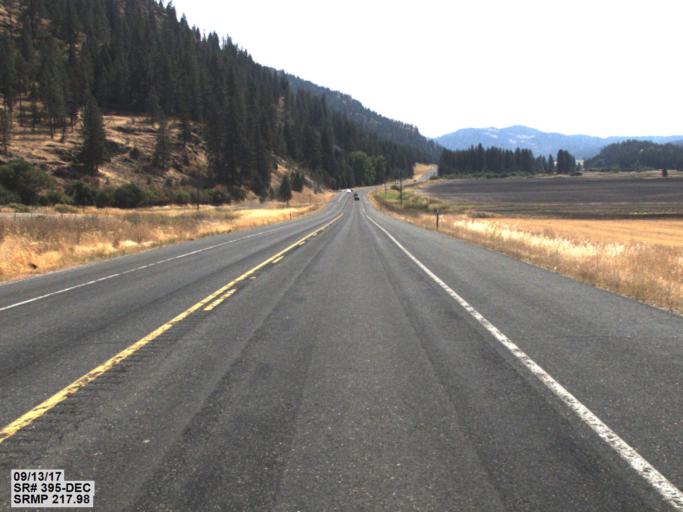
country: US
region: Washington
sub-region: Stevens County
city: Chewelah
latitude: 48.3875
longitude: -117.8440
